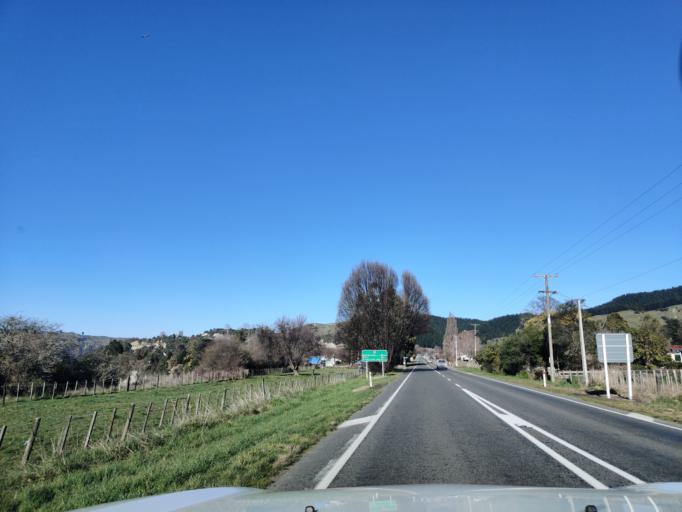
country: NZ
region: Manawatu-Wanganui
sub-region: Ruapehu District
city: Waiouru
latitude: -39.8125
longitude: 175.7849
